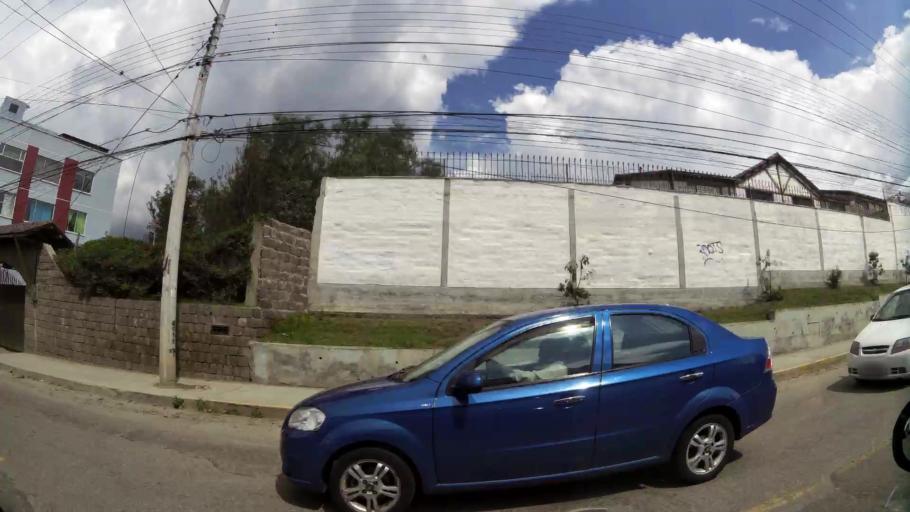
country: EC
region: Pichincha
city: Quito
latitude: -0.1057
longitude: -78.4564
